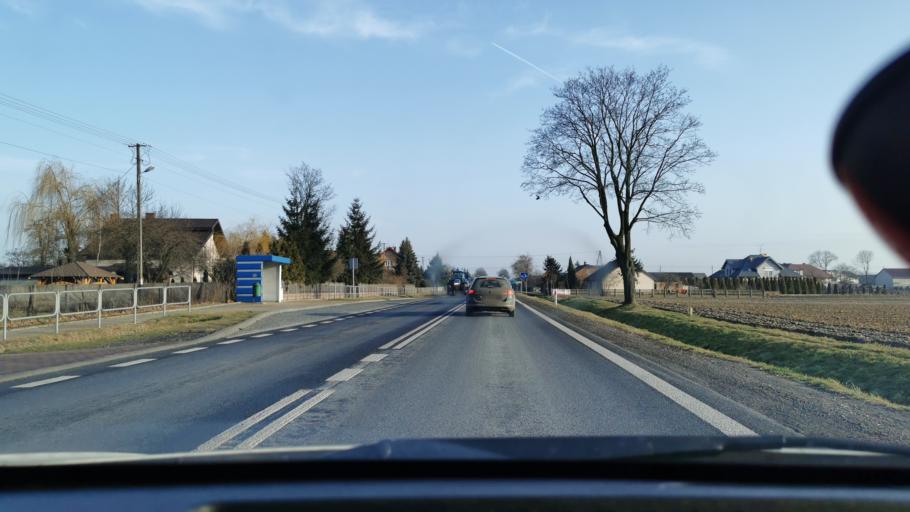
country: PL
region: Lodz Voivodeship
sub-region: Powiat sieradzki
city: Wroblew
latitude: 51.6313
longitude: 18.5475
